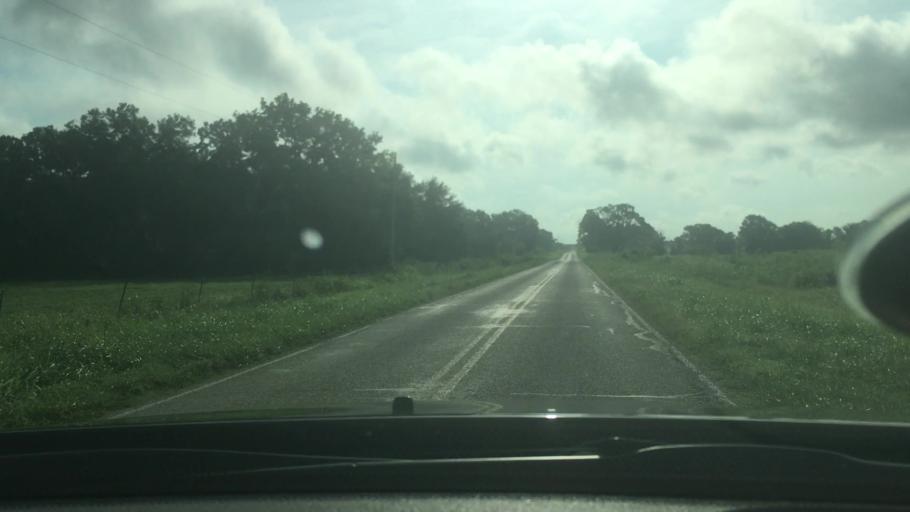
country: US
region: Oklahoma
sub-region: Pontotoc County
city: Ada
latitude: 34.6946
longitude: -96.5463
